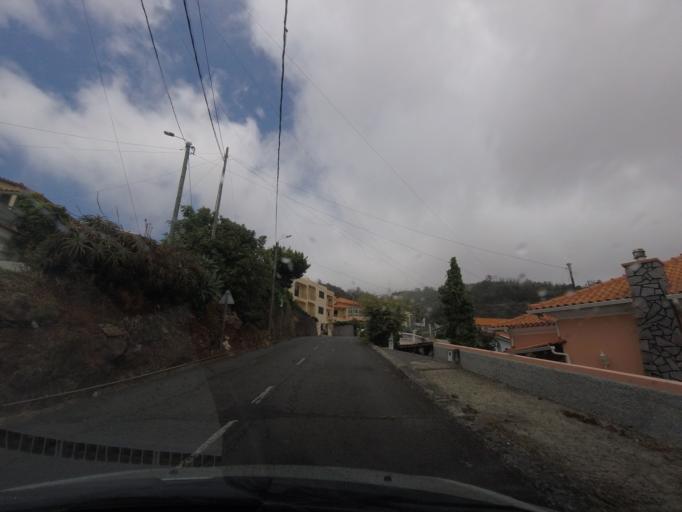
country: PT
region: Madeira
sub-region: Machico
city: Machico
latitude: 32.7047
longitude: -16.7762
